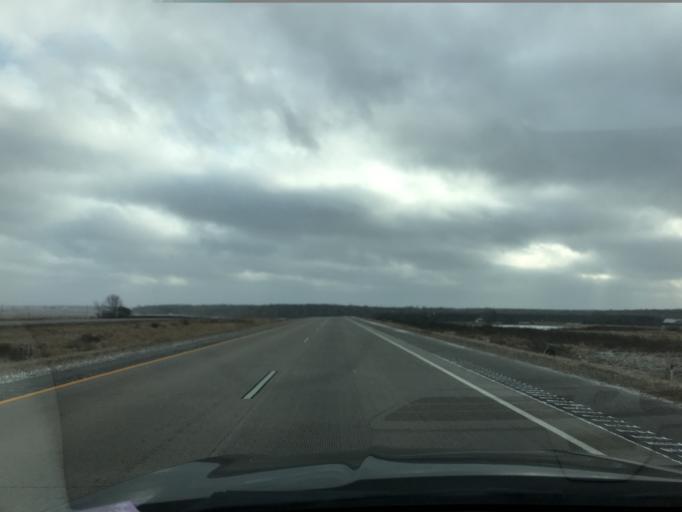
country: US
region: Wisconsin
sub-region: Wood County
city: Marshfield
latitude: 44.6171
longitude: -89.9737
